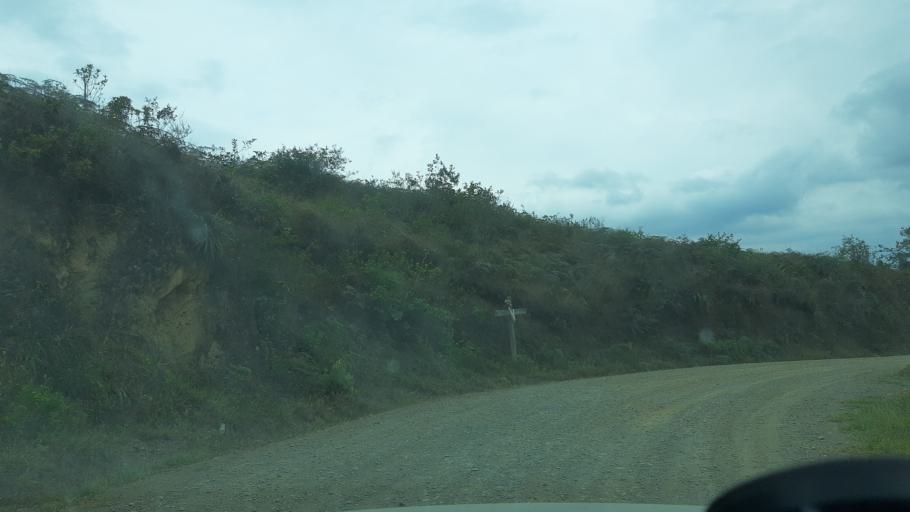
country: CO
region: Boyaca
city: Somondoco
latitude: 4.9815
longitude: -73.3765
